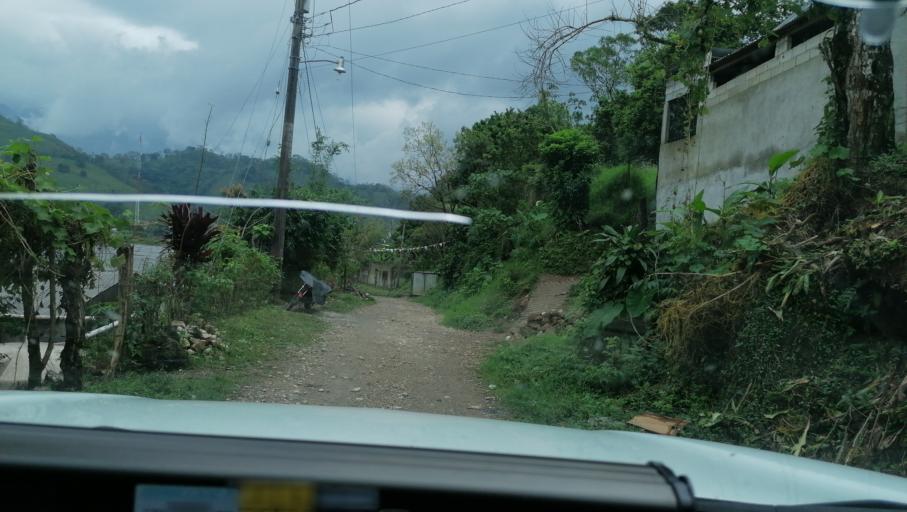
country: MX
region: Chiapas
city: Ixtacomitan
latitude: 17.3437
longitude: -93.1346
